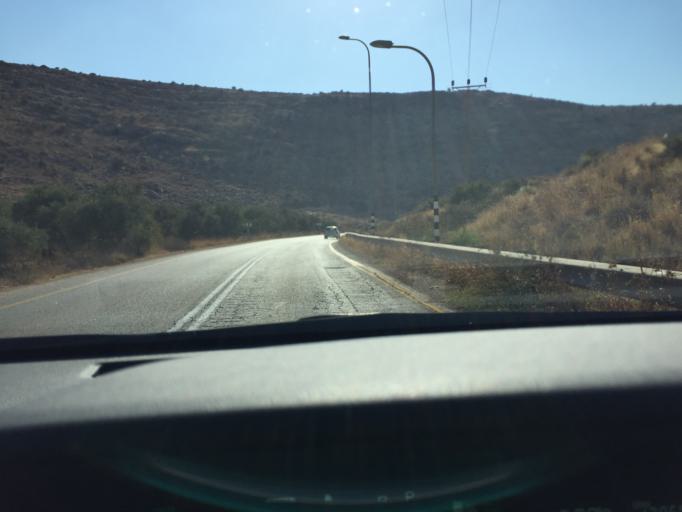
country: PS
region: West Bank
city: Al Lubban al Gharbi
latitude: 32.0487
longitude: 35.0440
